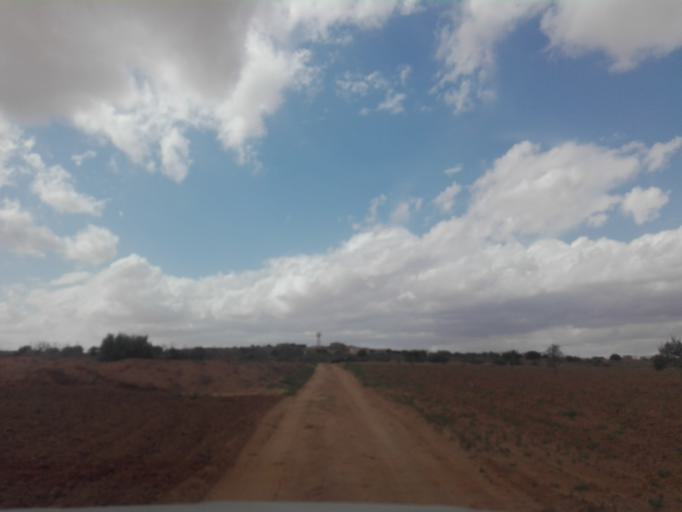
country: TN
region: Safaqis
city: Sfax
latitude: 34.7008
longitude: 10.4412
